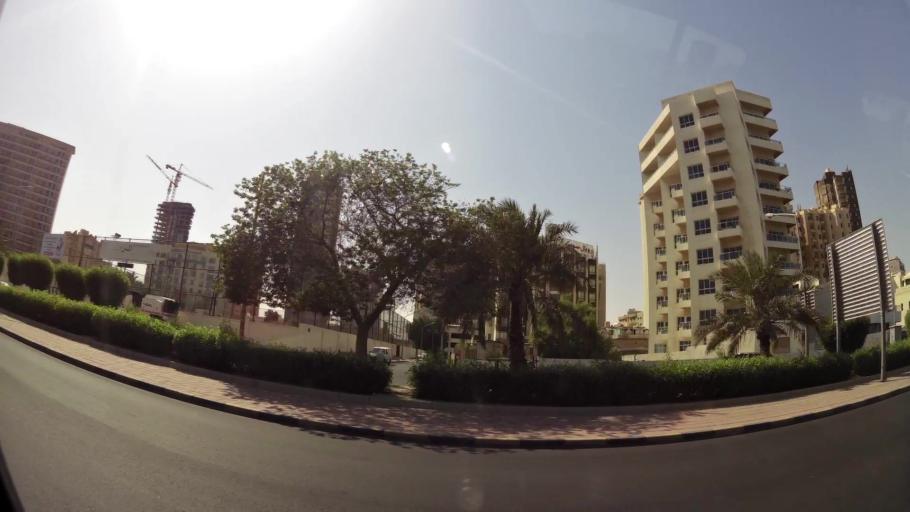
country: KW
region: Al Asimah
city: Ad Dasmah
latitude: 29.3705
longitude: 48.0098
